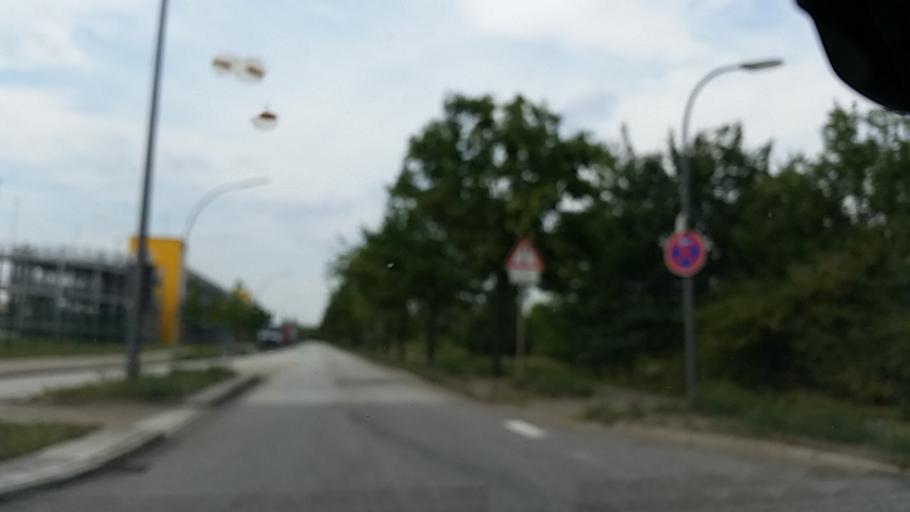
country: DE
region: Hamburg
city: Wandsbek
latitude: 53.4970
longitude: 10.1130
